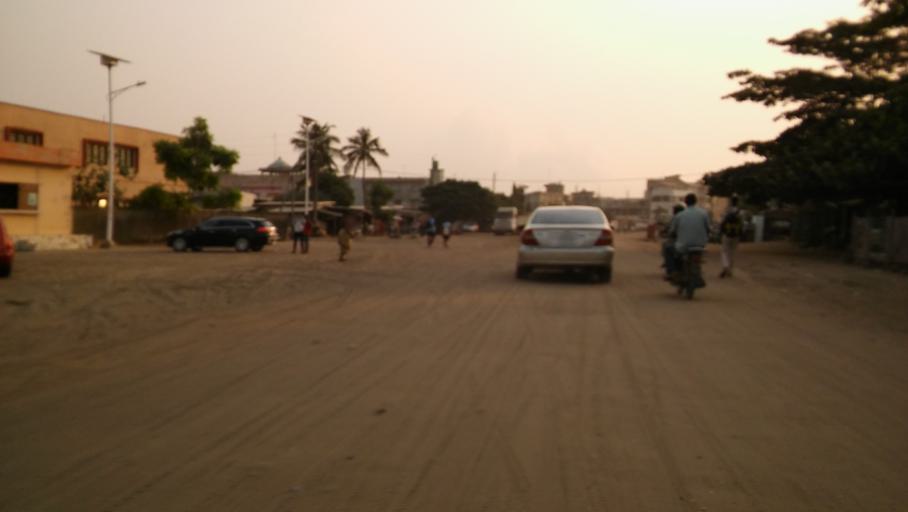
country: BJ
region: Littoral
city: Cotonou
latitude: 6.3907
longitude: 2.3786
